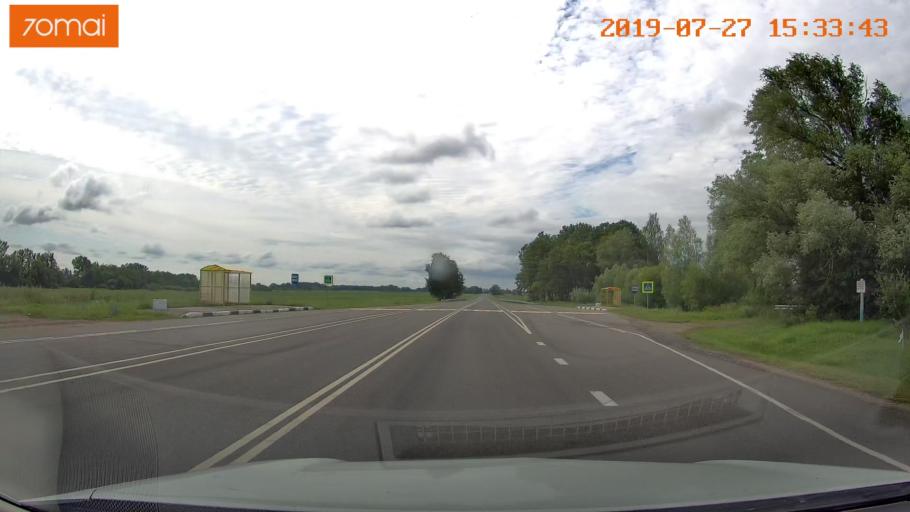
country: RU
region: Kaliningrad
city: Nesterov
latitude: 54.6122
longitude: 22.4440
